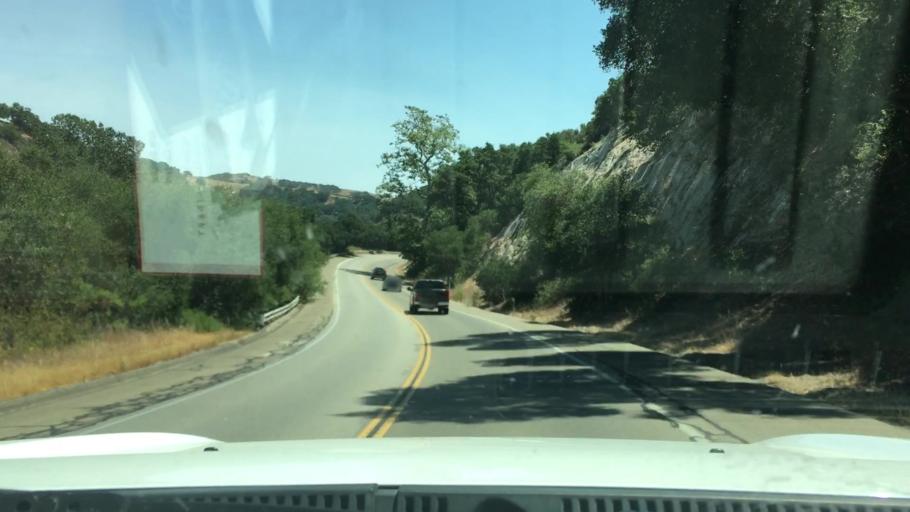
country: US
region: California
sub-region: San Luis Obispo County
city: Pismo Beach
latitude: 35.1612
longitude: -120.6344
